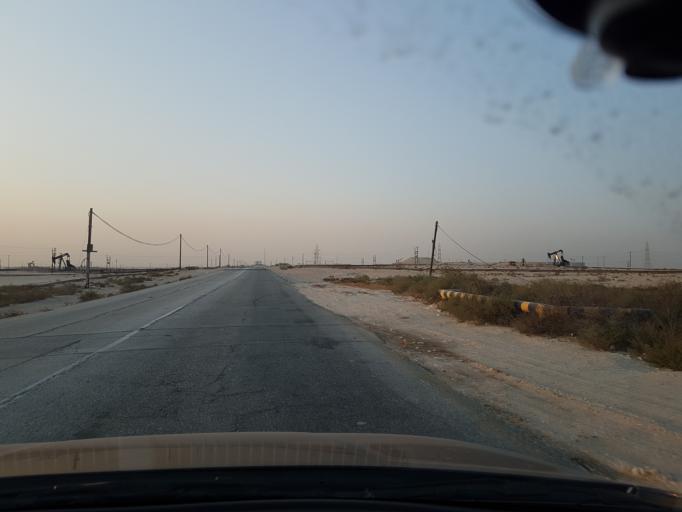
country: BH
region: Central Governorate
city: Dar Kulayb
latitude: 26.0615
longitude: 50.5540
